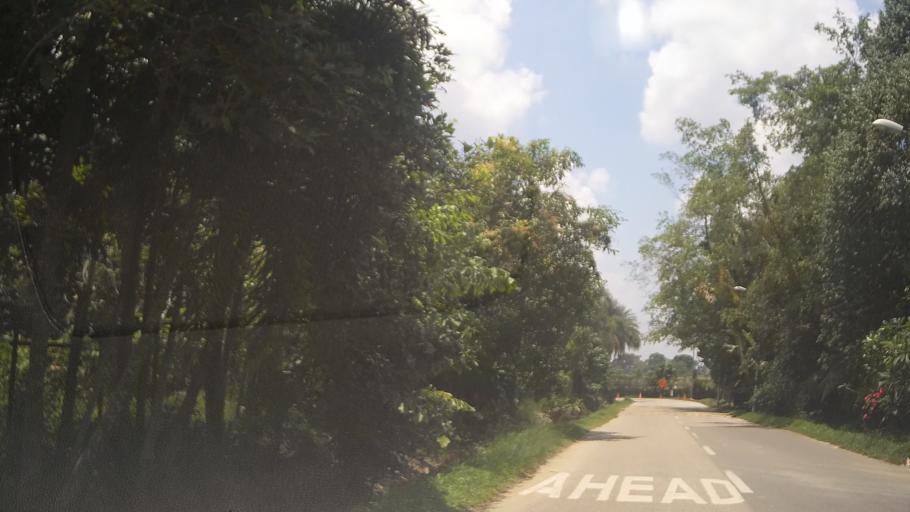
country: MY
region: Johor
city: Kampung Pasir Gudang Baru
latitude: 1.3966
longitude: 103.8637
